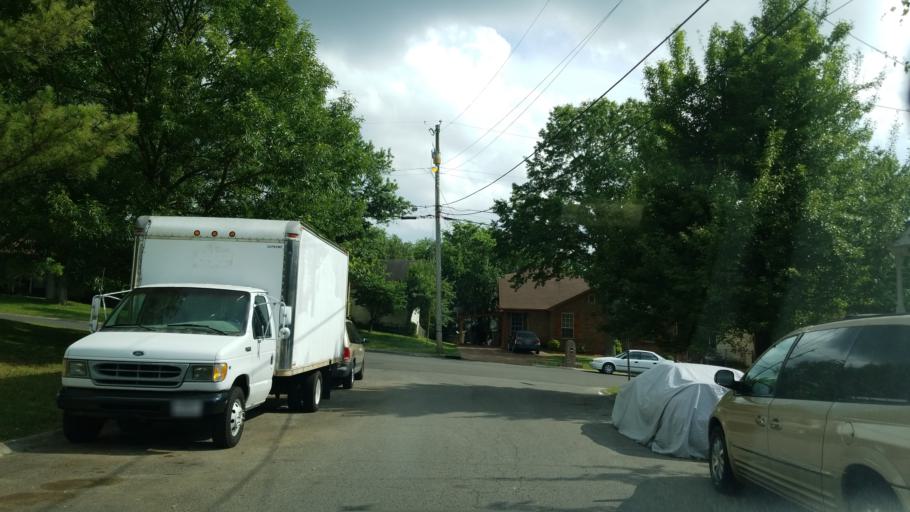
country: US
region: Tennessee
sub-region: Rutherford County
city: La Vergne
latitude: 36.0702
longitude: -86.6083
